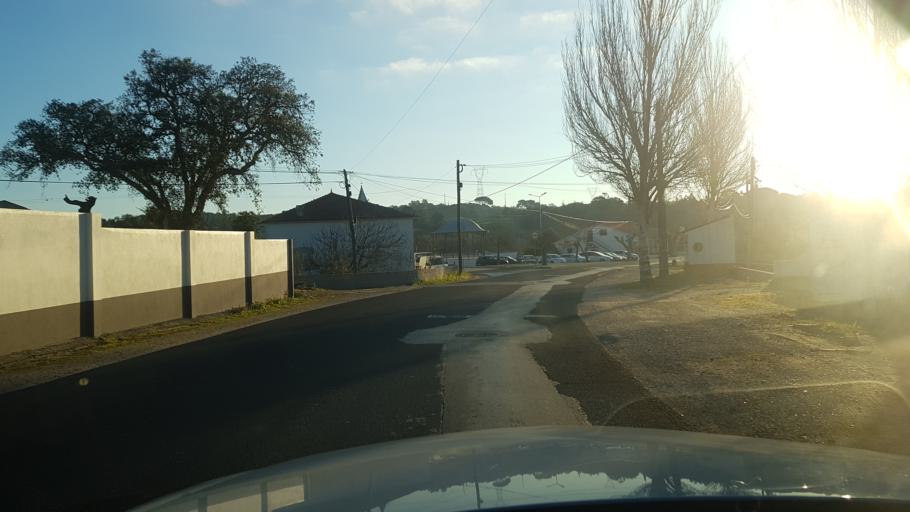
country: PT
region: Santarem
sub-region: Torres Novas
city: Torres Novas
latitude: 39.5533
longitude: -8.5546
